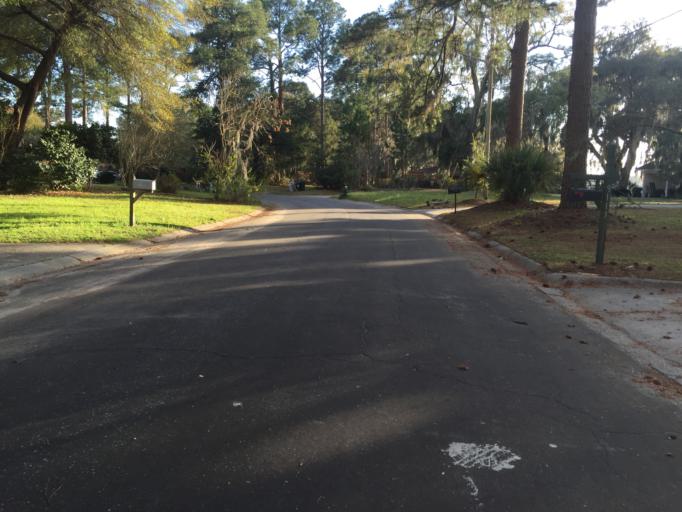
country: US
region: Georgia
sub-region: Chatham County
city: Montgomery
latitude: 31.9814
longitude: -81.1120
